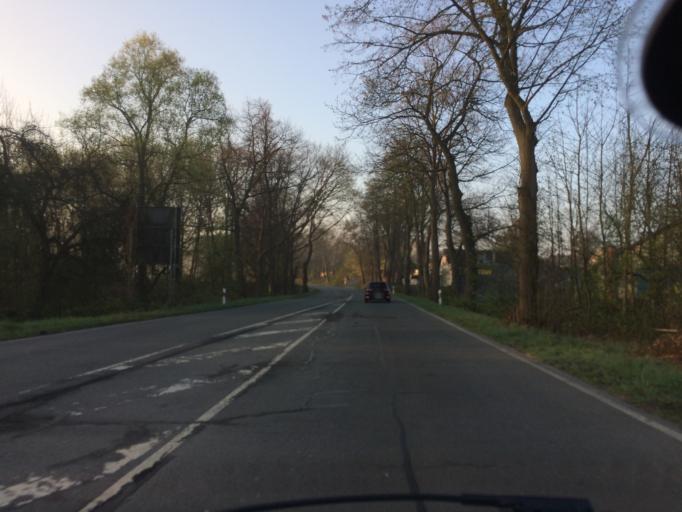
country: DE
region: North Rhine-Westphalia
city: Hattingen
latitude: 51.4219
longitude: 7.1680
